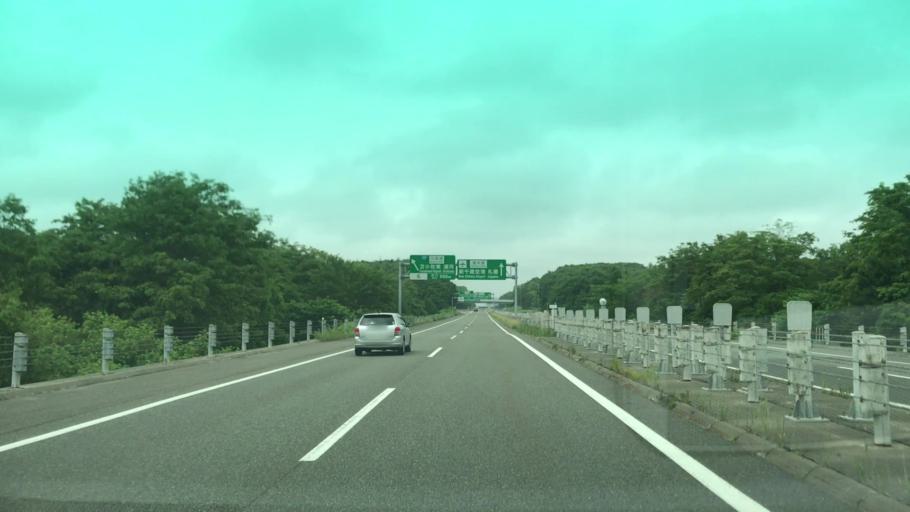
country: JP
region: Hokkaido
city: Tomakomai
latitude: 42.7055
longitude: 141.6522
